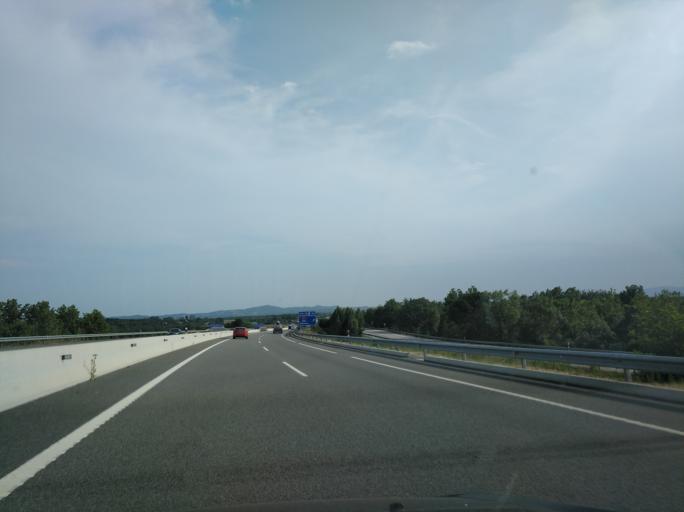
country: ES
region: Catalonia
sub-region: Provincia de Girona
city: Sils
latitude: 41.8184
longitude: 2.7638
